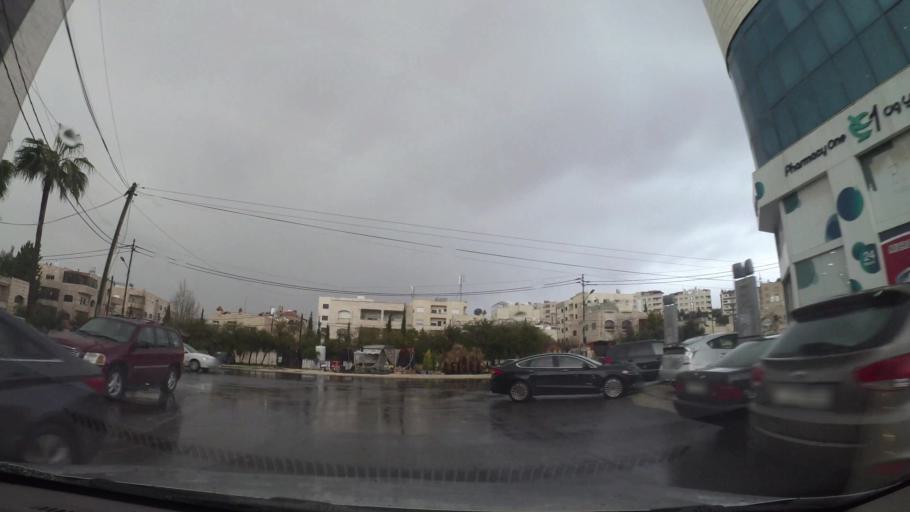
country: JO
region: Amman
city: Umm as Summaq
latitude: 31.8988
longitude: 35.8583
